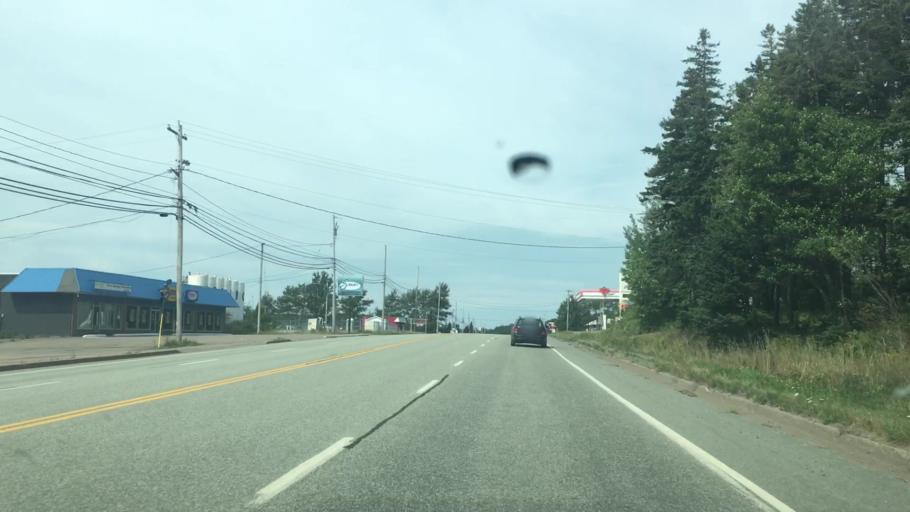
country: CA
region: Nova Scotia
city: Port Hawkesbury
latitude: 45.6399
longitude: -61.3861
